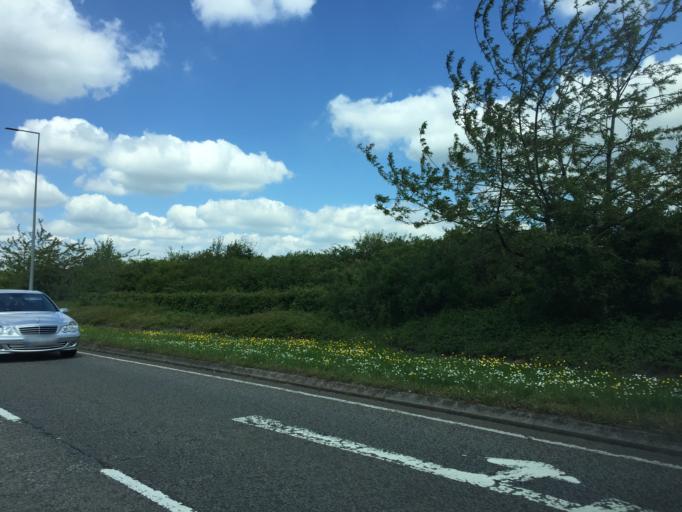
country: GB
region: England
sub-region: Milton Keynes
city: Simpson
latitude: 52.0252
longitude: -0.7043
